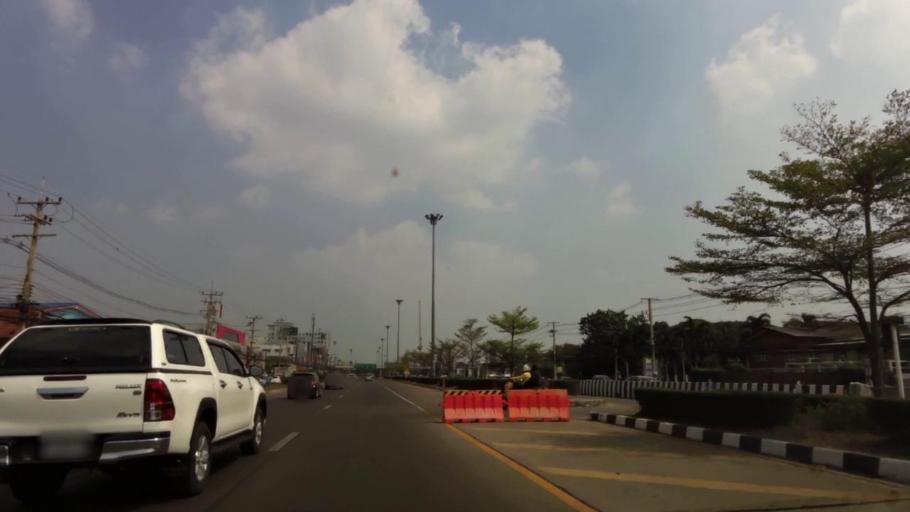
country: TH
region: Phra Nakhon Si Ayutthaya
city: Phra Nakhon Si Ayutthaya
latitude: 14.3541
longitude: 100.5932
